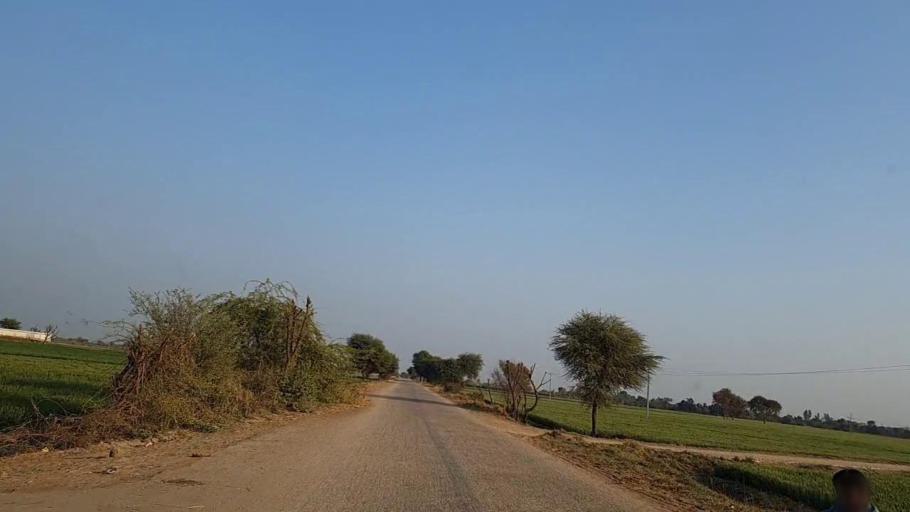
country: PK
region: Sindh
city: Sakrand
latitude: 26.0434
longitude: 68.4230
